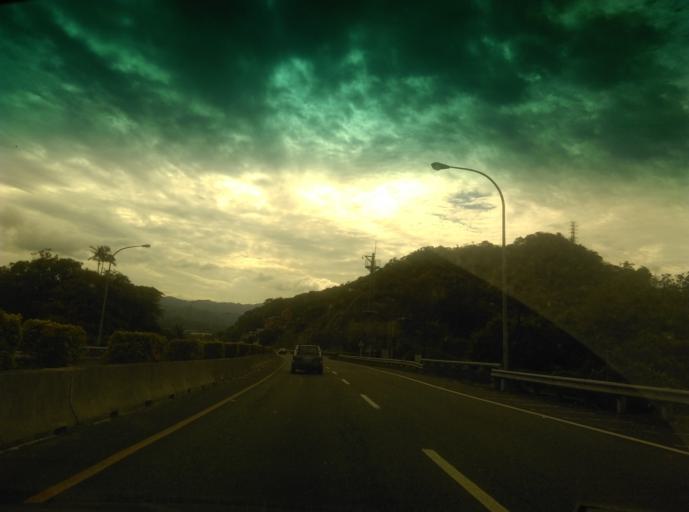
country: TW
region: Taiwan
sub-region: Keelung
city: Keelung
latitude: 25.1162
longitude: 121.7290
